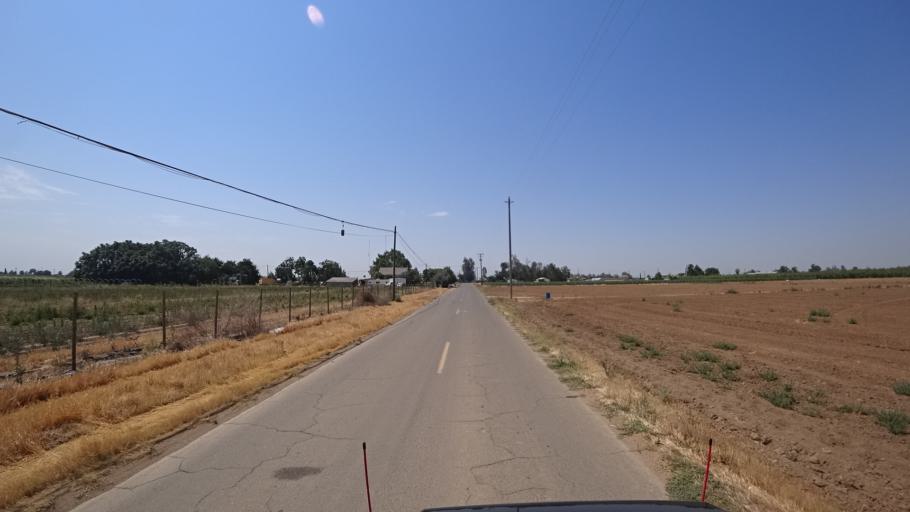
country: US
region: California
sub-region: Fresno County
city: West Park
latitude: 36.7173
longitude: -119.8357
